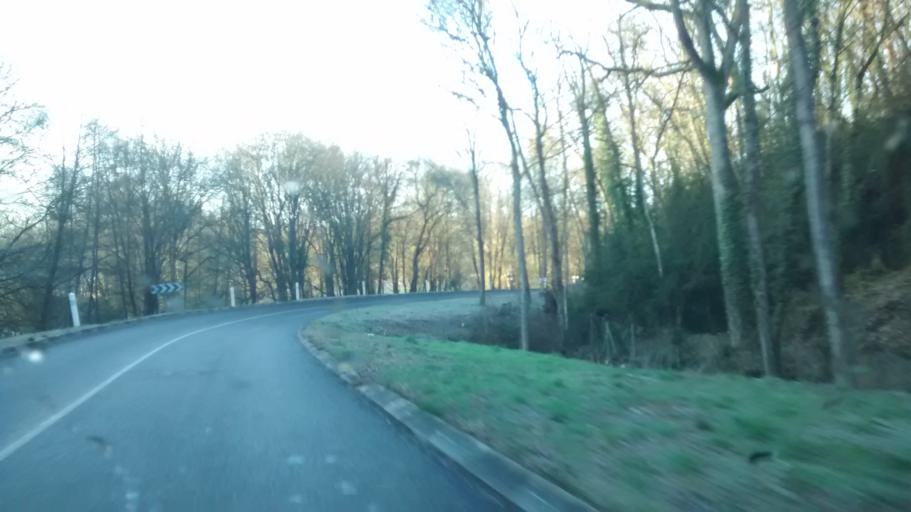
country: FR
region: Centre
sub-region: Departement d'Indre-et-Loire
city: Esvres
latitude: 47.2804
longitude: 0.7985
